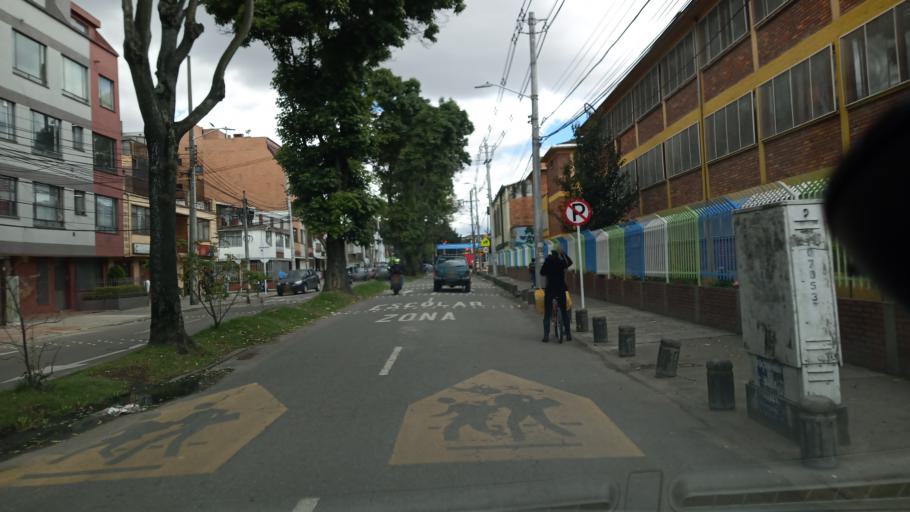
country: CO
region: Bogota D.C.
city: Bogota
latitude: 4.6710
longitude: -74.1382
